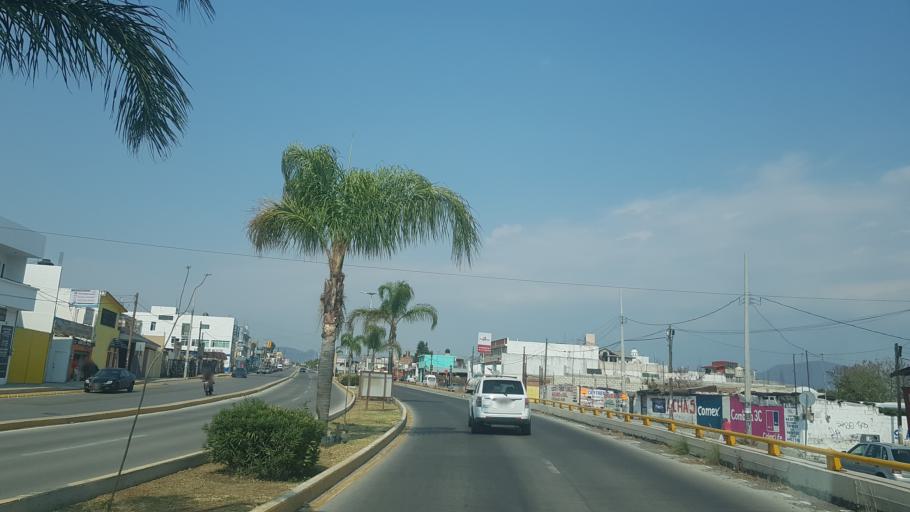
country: MX
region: Puebla
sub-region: Atlixco
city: El Encanto del Cerril
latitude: 18.9176
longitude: -98.4228
